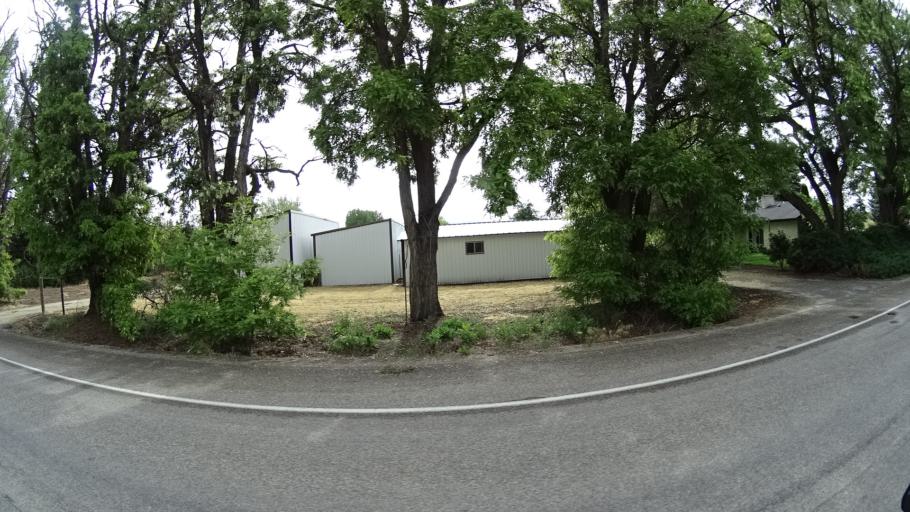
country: US
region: Idaho
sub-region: Ada County
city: Eagle
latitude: 43.7016
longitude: -116.3791
